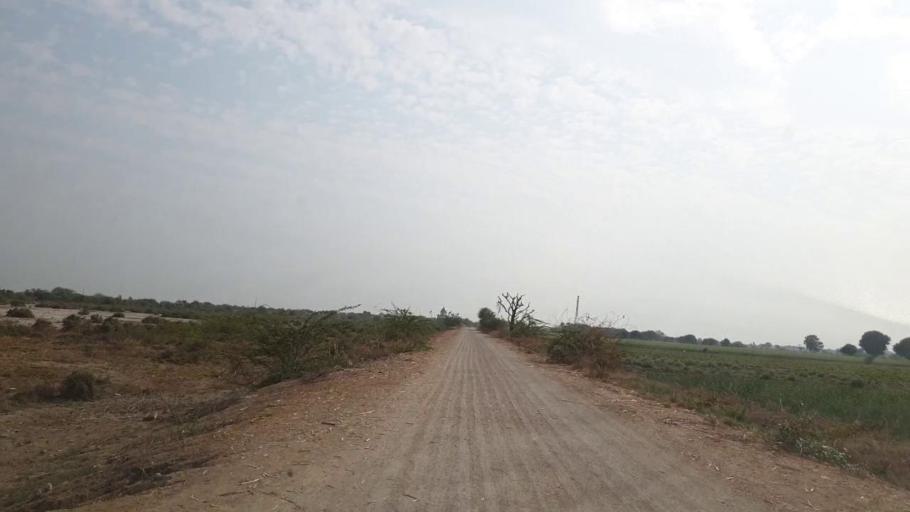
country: PK
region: Sindh
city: Mirpur Khas
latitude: 25.5583
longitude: 69.1697
